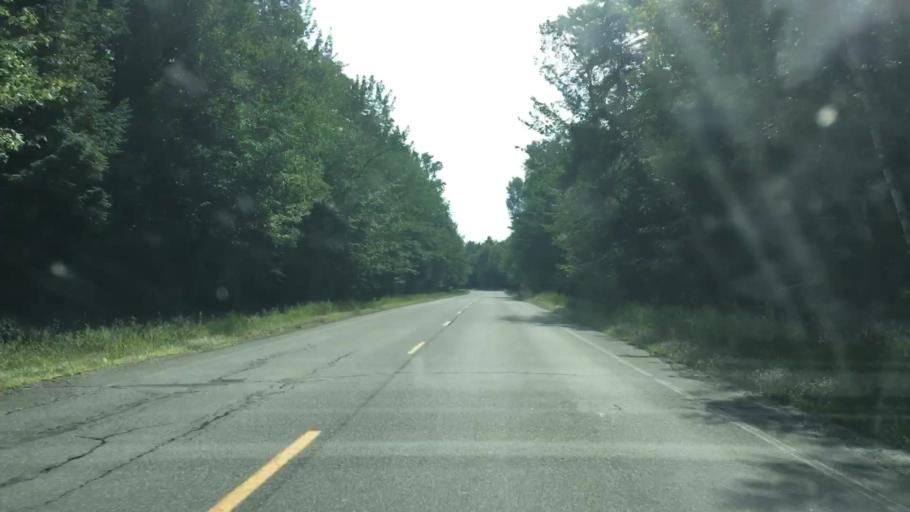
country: US
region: Maine
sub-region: Penobscot County
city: Lincoln
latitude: 45.3816
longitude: -68.5455
